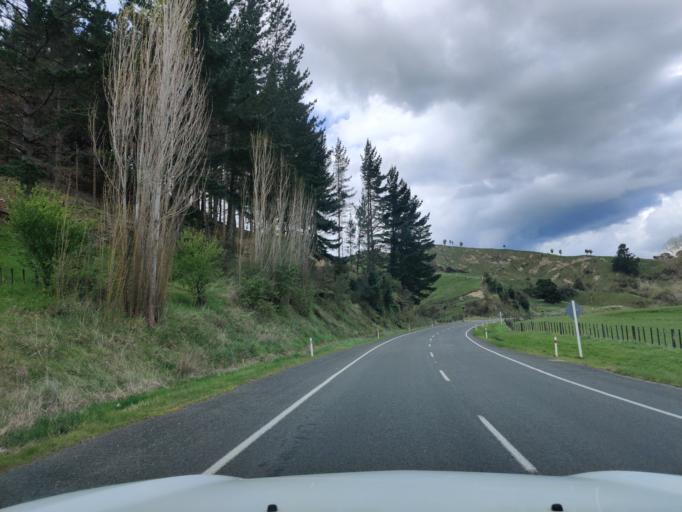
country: NZ
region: Manawatu-Wanganui
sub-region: Wanganui District
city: Wanganui
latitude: -39.8470
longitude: 175.1282
